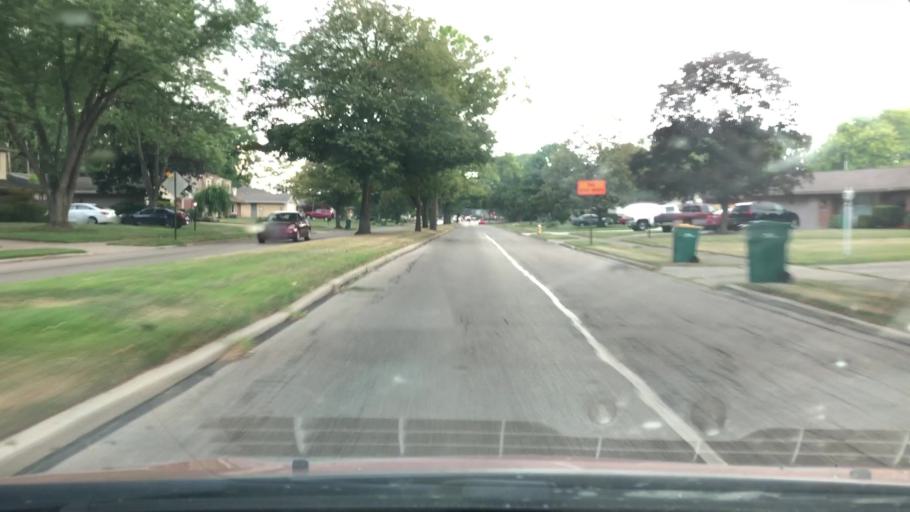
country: US
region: Ohio
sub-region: Montgomery County
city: Centerville
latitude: 39.6627
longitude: -84.1233
